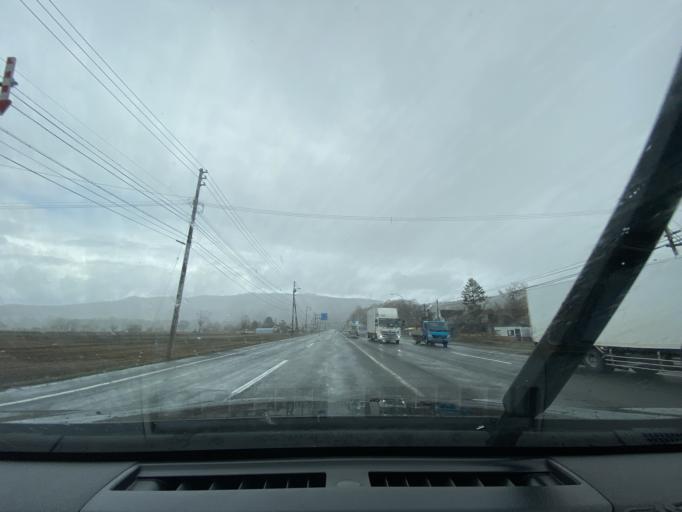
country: JP
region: Hokkaido
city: Fukagawa
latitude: 43.7237
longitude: 142.1849
